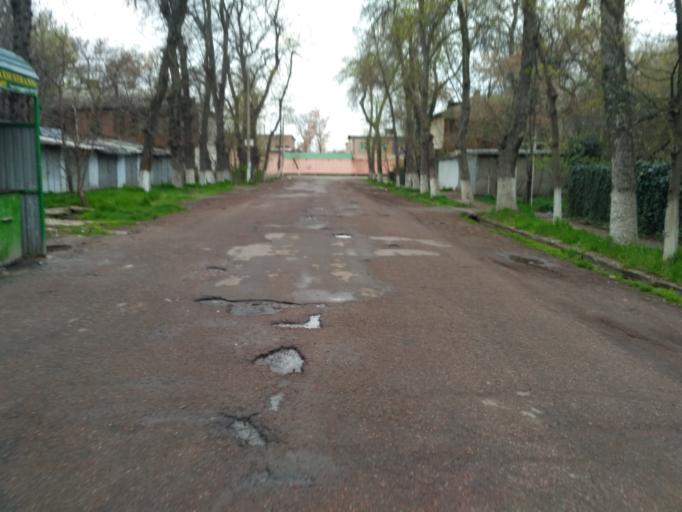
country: UZ
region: Toshkent Shahri
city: Tashkent
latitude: 41.2690
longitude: 69.2781
